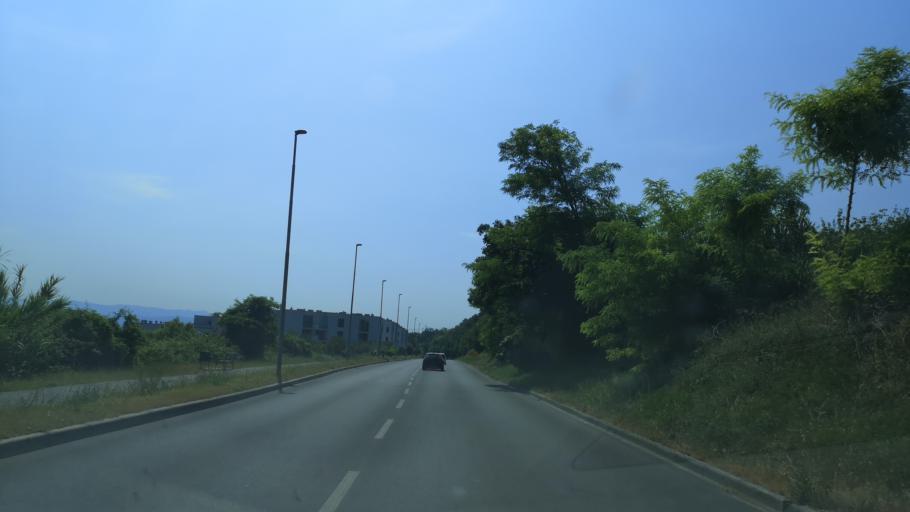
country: SI
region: Koper-Capodistria
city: Koper
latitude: 45.5420
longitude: 13.6973
